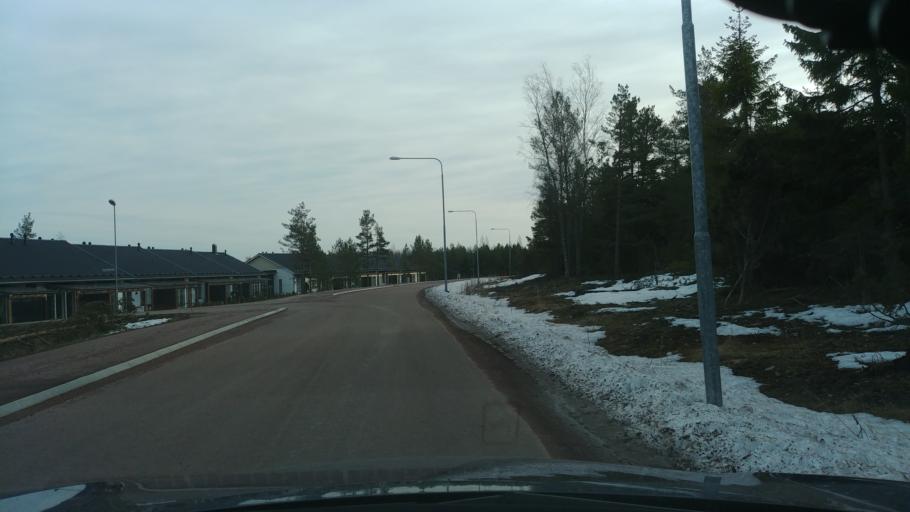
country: AX
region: Mariehamns stad
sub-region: Mariehamn
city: Mariehamn
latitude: 60.0985
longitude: 19.8940
